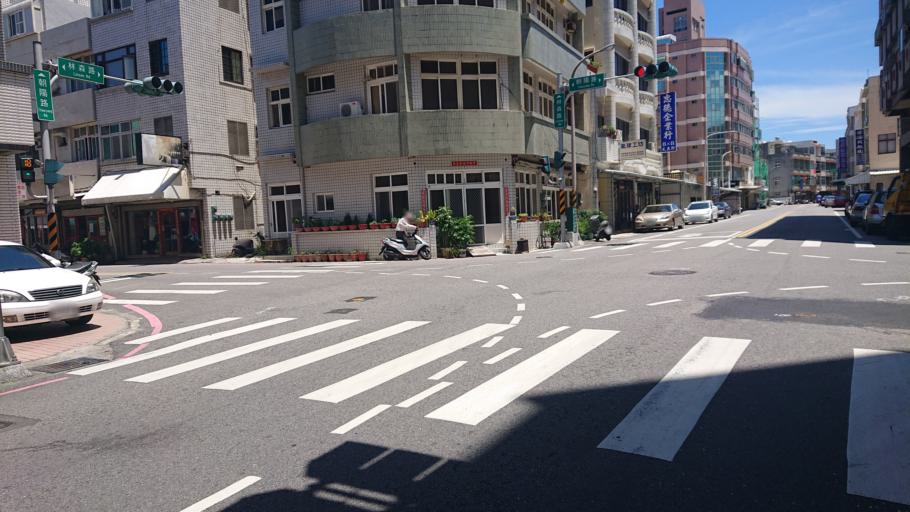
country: TW
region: Taiwan
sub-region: Penghu
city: Ma-kung
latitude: 23.5733
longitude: 119.5772
